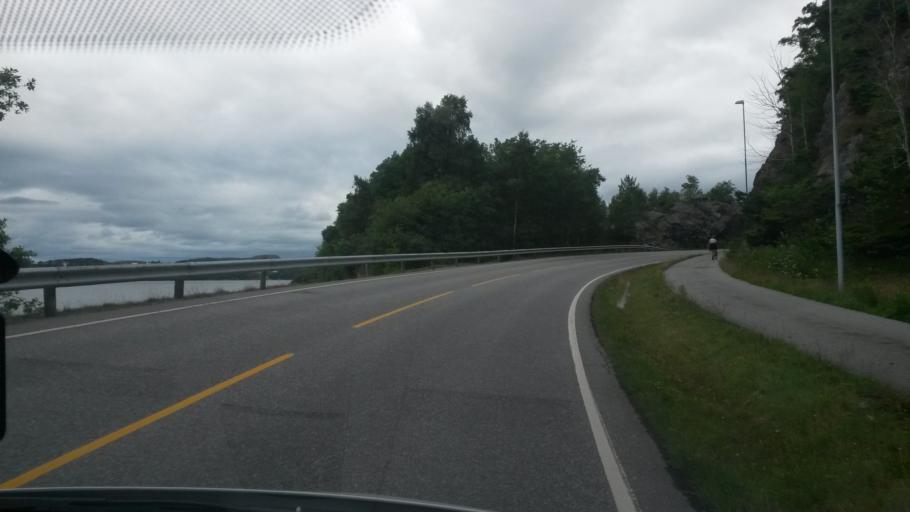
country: NO
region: Rogaland
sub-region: Sandnes
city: Sandnes
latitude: 58.8731
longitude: 5.7644
